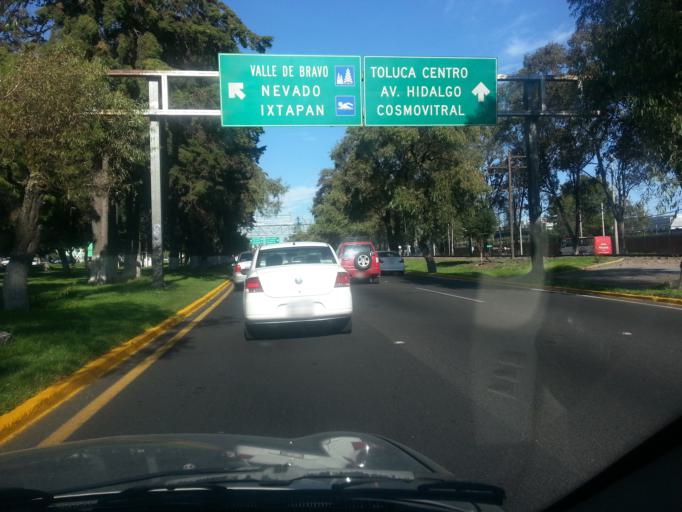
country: MX
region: Mexico
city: Toluca
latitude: 19.2882
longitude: -99.6235
